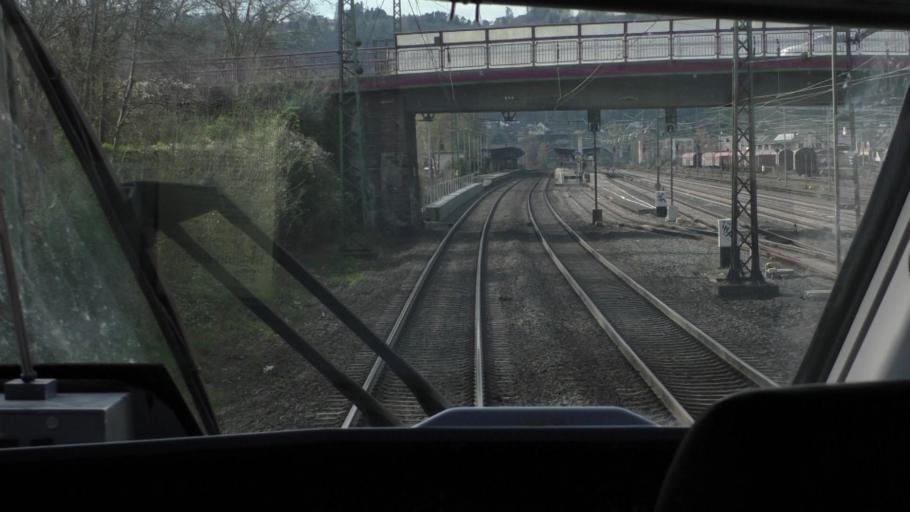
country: DE
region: Rheinland-Pfalz
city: Andernach
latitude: 50.4326
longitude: 7.4111
